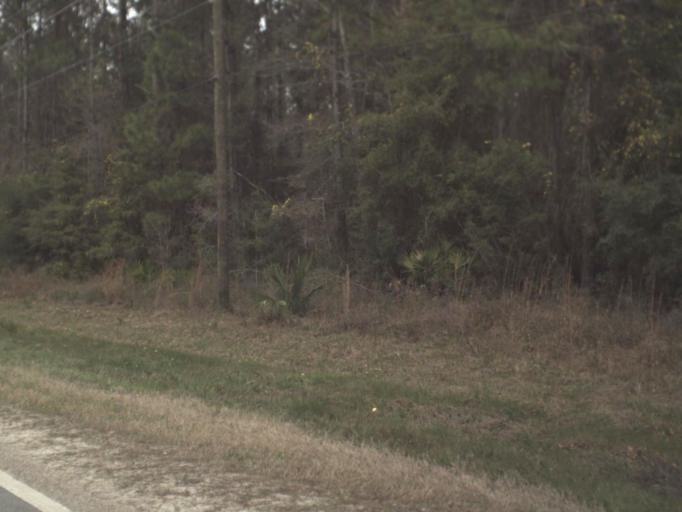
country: US
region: Florida
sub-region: Leon County
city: Woodville
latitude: 30.1913
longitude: -84.2128
